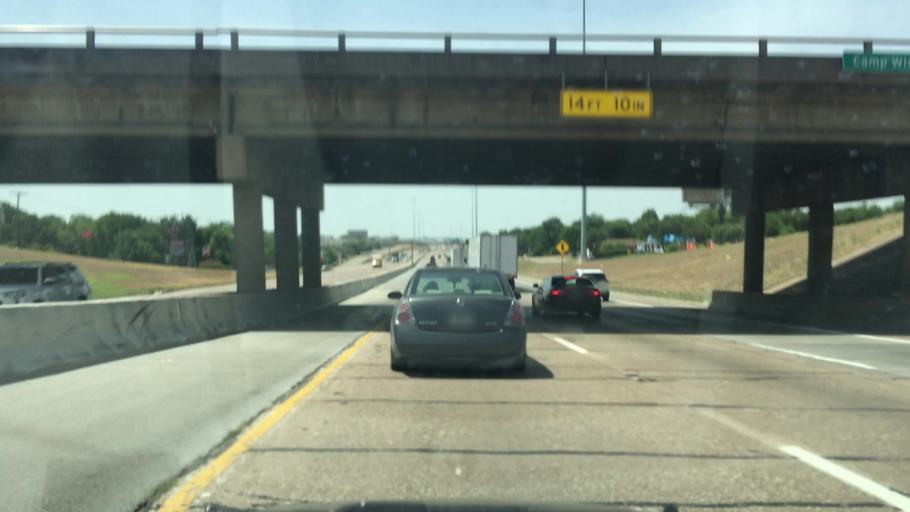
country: US
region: Texas
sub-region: Dallas County
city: DeSoto
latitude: 32.6624
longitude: -96.8230
